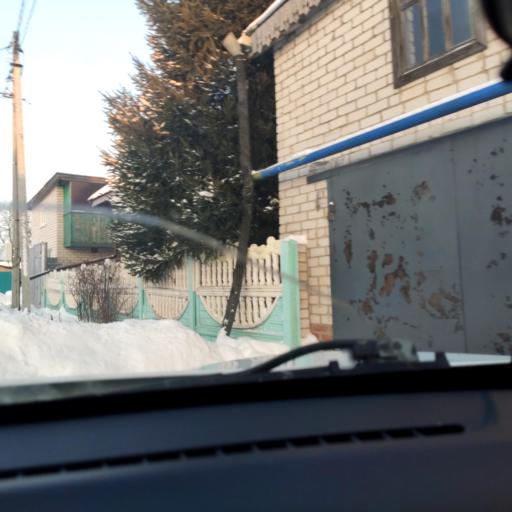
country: RU
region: Tatarstan
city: Staroye Arakchino
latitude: 55.8776
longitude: 49.0255
